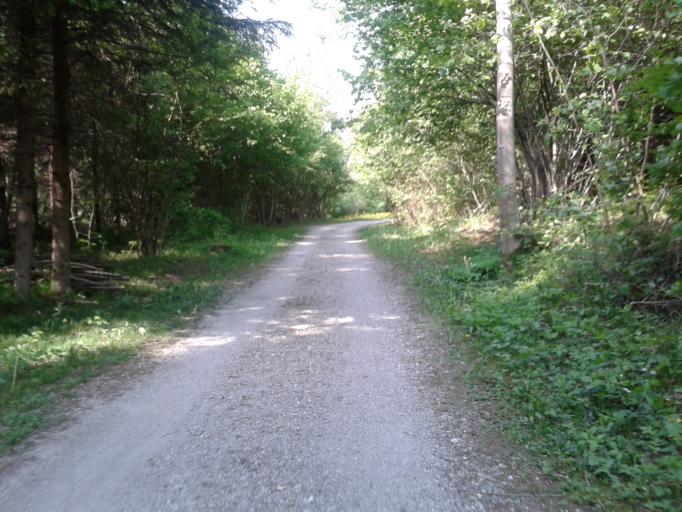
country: IT
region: Trentino-Alto Adige
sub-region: Provincia di Trento
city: Condino
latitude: 45.8669
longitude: 10.5836
